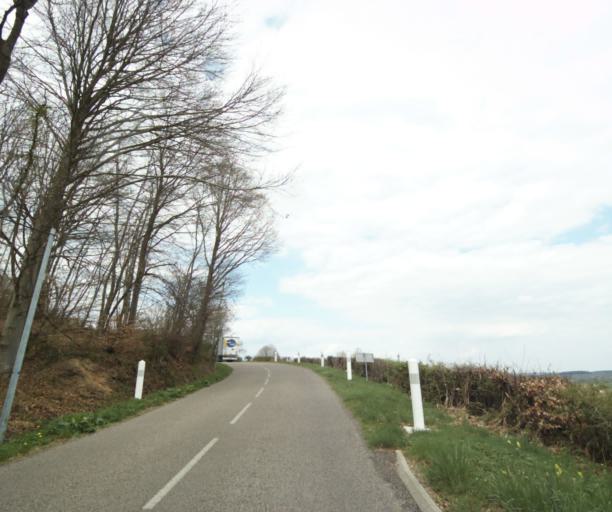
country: FR
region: Bourgogne
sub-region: Departement de Saone-et-Loire
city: Ciry-le-Noble
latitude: 46.5451
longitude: 4.3104
